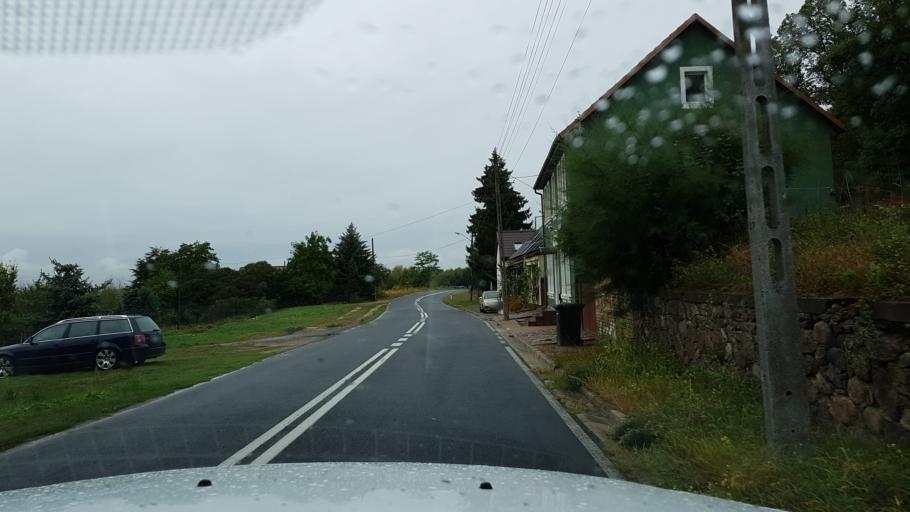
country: PL
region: West Pomeranian Voivodeship
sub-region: Powiat gryfinski
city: Cedynia
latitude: 52.8316
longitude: 14.1397
